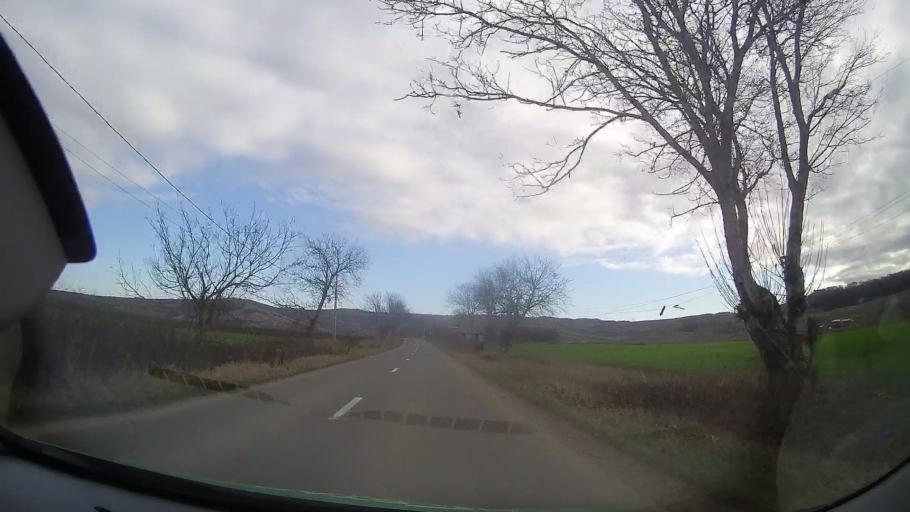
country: RO
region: Mures
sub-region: Comuna Iernut
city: Iernut
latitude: 46.4886
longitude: 24.2472
